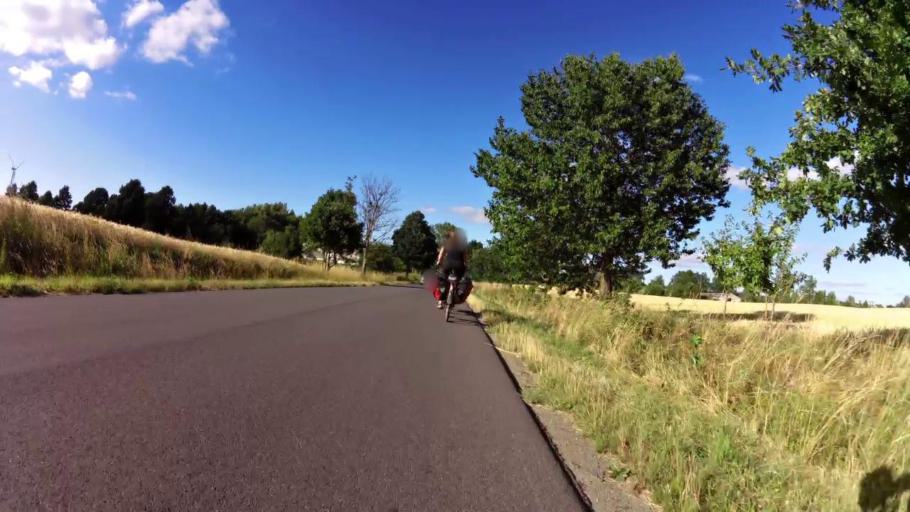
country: PL
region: West Pomeranian Voivodeship
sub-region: Powiat swidwinski
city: Swidwin
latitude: 53.6940
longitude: 15.7812
